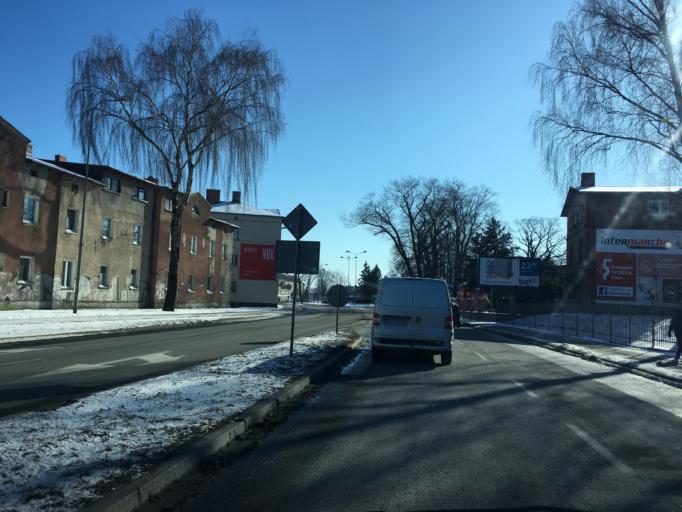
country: PL
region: Pomeranian Voivodeship
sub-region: Slupsk
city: Slupsk
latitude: 54.4651
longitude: 17.0112
